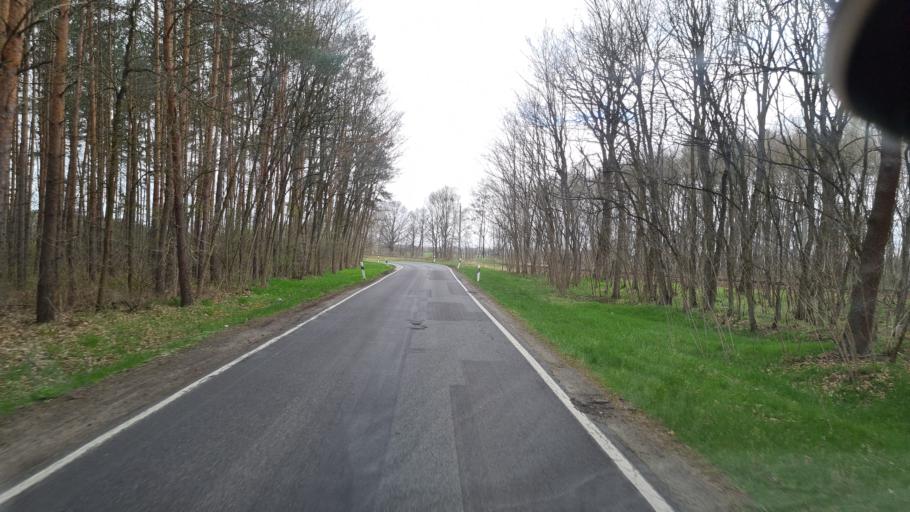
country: DE
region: Brandenburg
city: Schwarzbach
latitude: 51.4556
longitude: 13.9033
